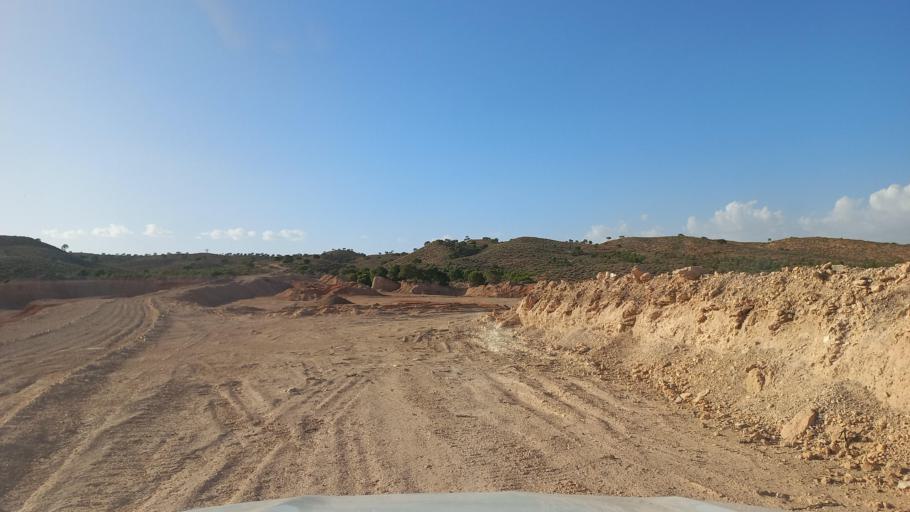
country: TN
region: Al Qasrayn
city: Sbiba
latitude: 35.3656
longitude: 8.9957
